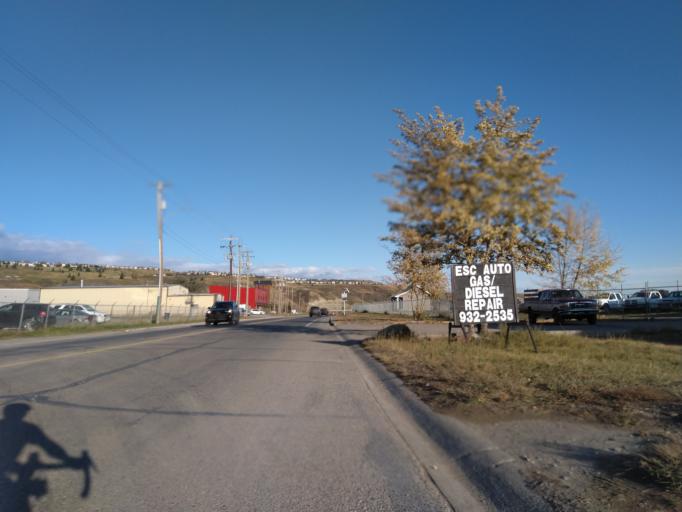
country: CA
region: Alberta
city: Cochrane
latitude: 51.1832
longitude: -114.4576
